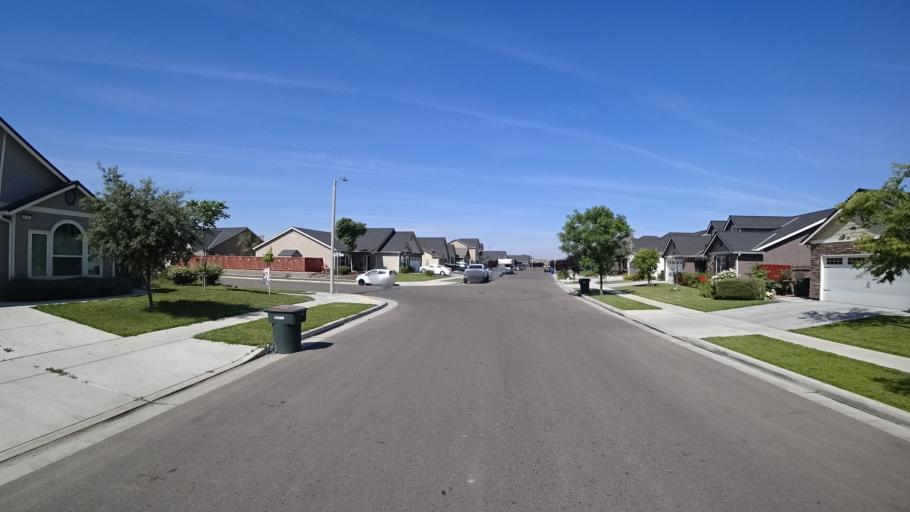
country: US
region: California
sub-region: Kings County
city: Hanford
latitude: 36.3378
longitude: -119.6774
